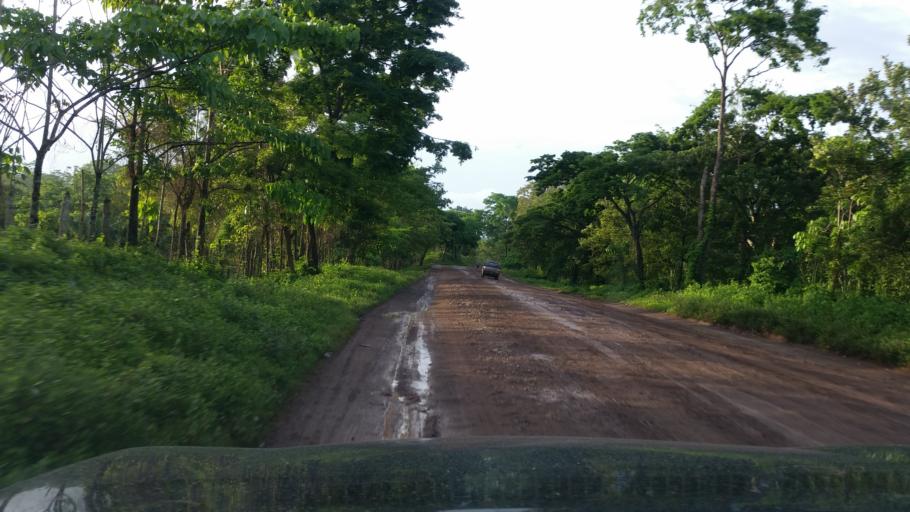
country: NI
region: Atlantico Norte (RAAN)
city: Siuna
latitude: 13.3478
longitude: -84.8897
